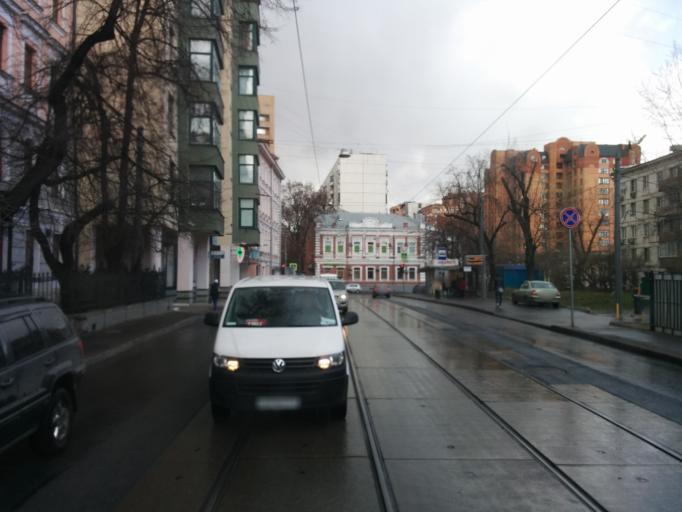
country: RU
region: Moscow
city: Mar'ina Roshcha
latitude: 55.7840
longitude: 37.6013
